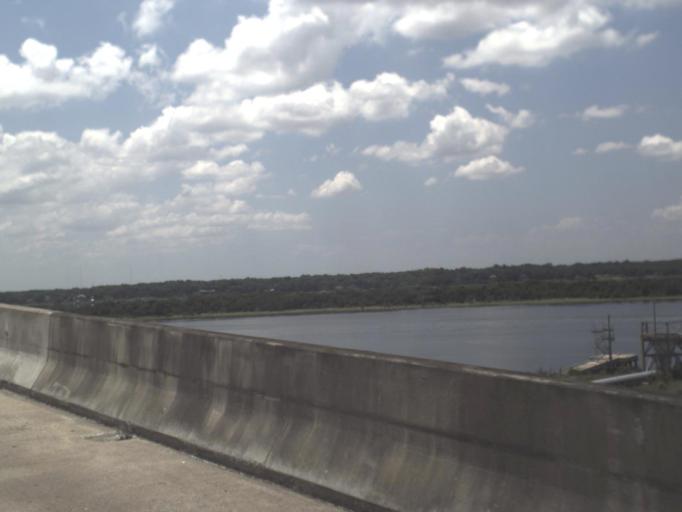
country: US
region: Florida
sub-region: Duval County
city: Jacksonville
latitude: 30.3903
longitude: -81.5596
